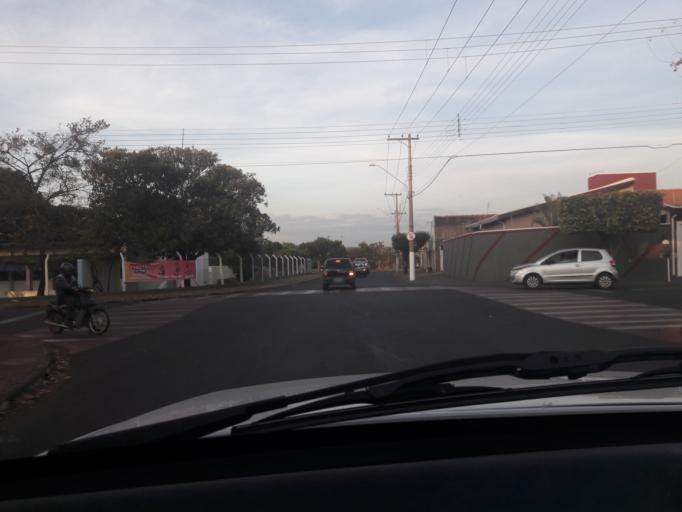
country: BR
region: Sao Paulo
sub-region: Moji-Guacu
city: Mogi-Gaucu
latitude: -22.3456
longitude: -46.9354
